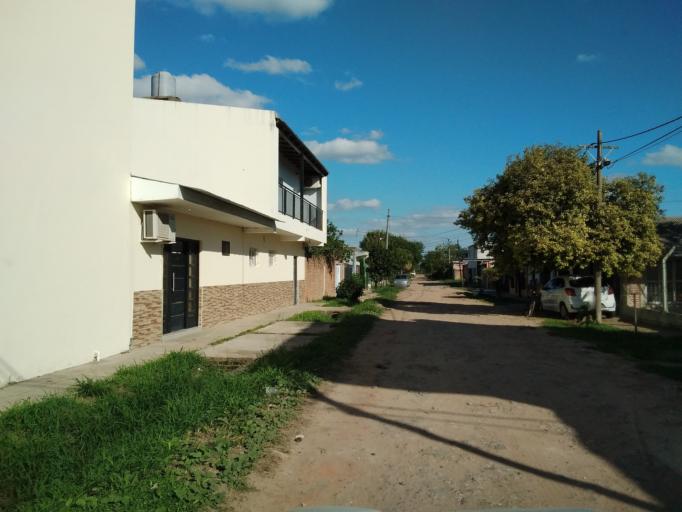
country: AR
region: Corrientes
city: Corrientes
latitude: -27.4607
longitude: -58.7762
